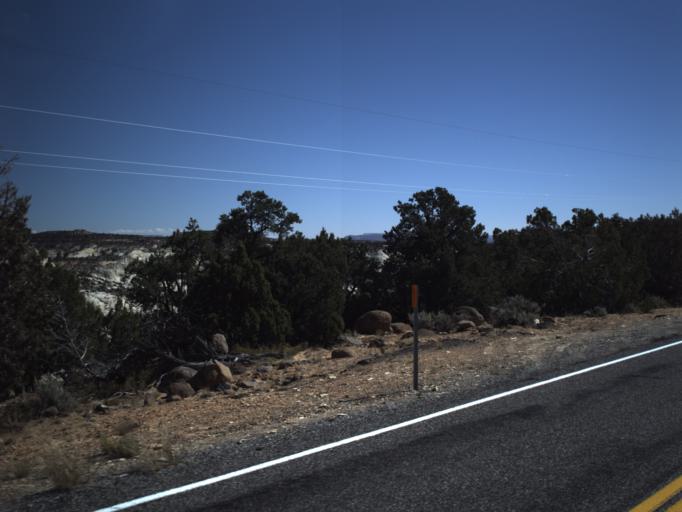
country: US
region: Utah
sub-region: Wayne County
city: Loa
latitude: 37.8620
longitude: -111.4385
